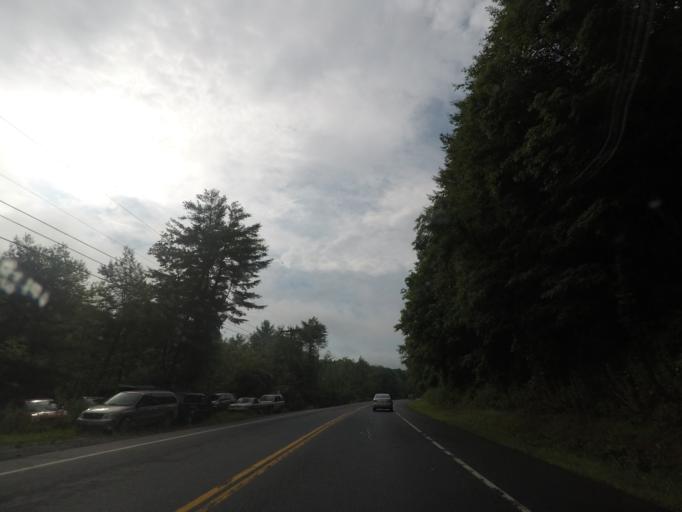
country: US
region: New York
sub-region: Rensselaer County
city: Nassau
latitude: 42.5080
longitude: -73.5630
